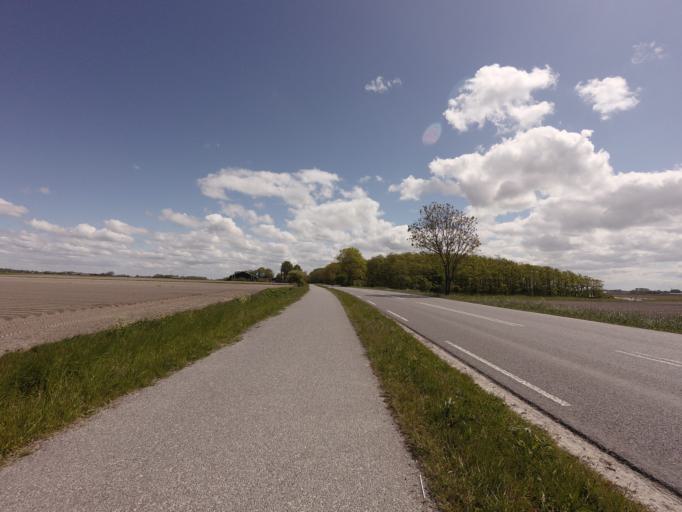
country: NL
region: Friesland
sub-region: Gemeente Harlingen
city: Harlingen
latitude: 53.1379
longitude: 5.4505
